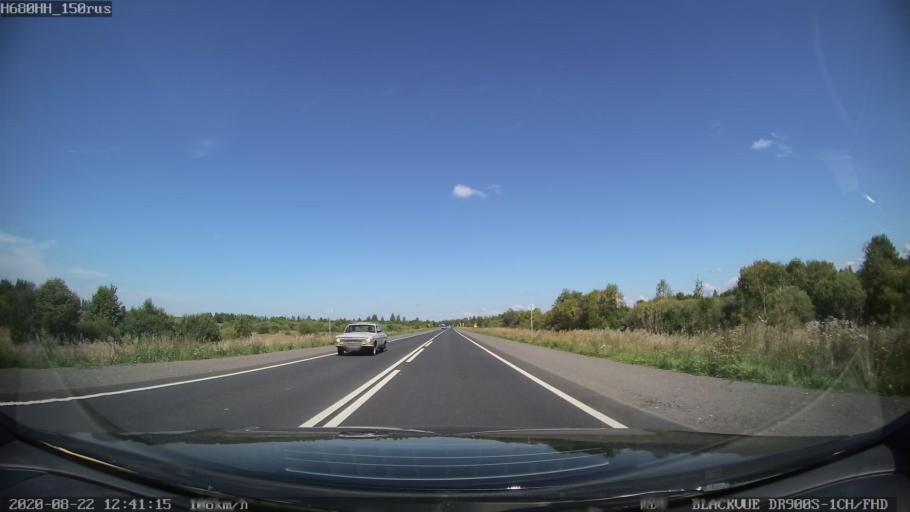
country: RU
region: Tverskaya
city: Rameshki
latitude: 57.3457
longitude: 36.0982
